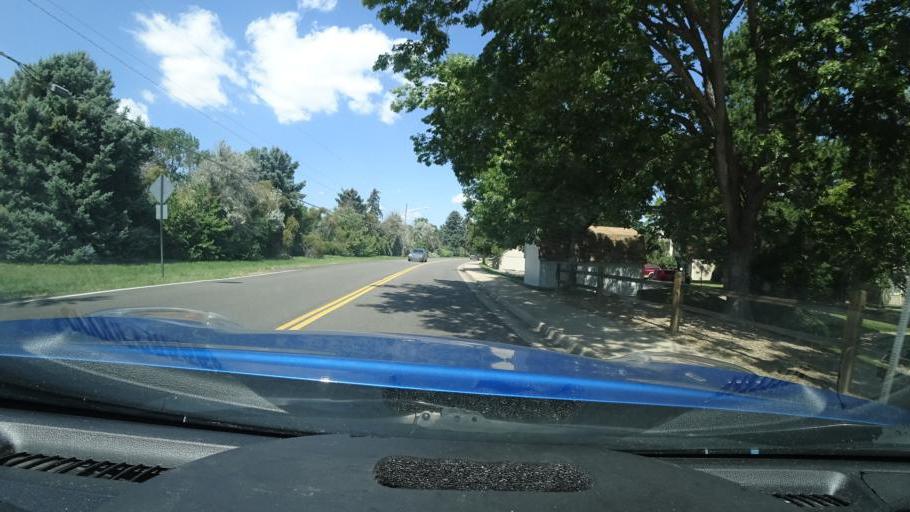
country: US
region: Colorado
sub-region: Arapahoe County
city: Glendale
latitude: 39.7063
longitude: -104.8911
